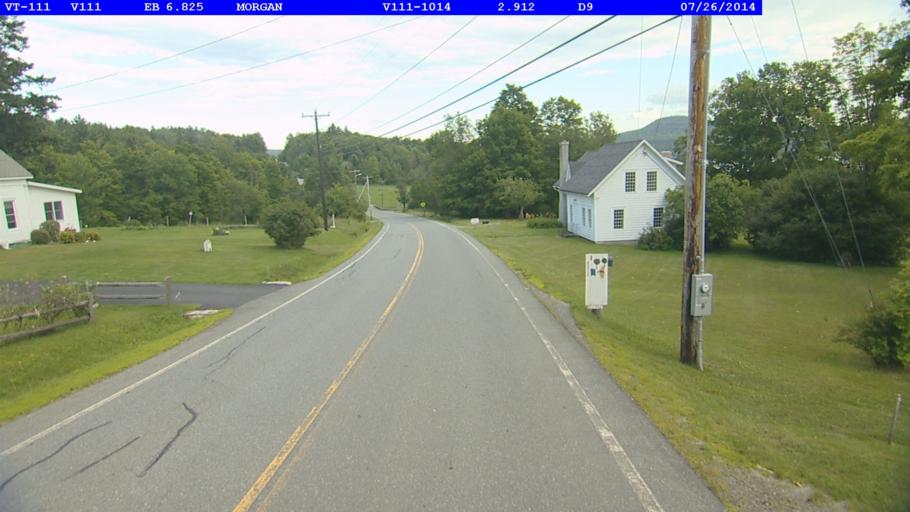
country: US
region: Vermont
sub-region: Orleans County
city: Newport
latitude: 44.9124
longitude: -72.0132
